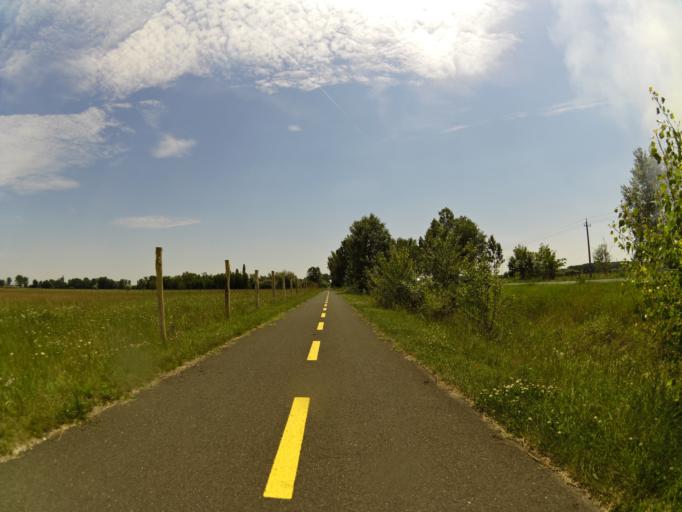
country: HU
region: Csongrad
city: Balastya
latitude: 46.4417
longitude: 20.0029
